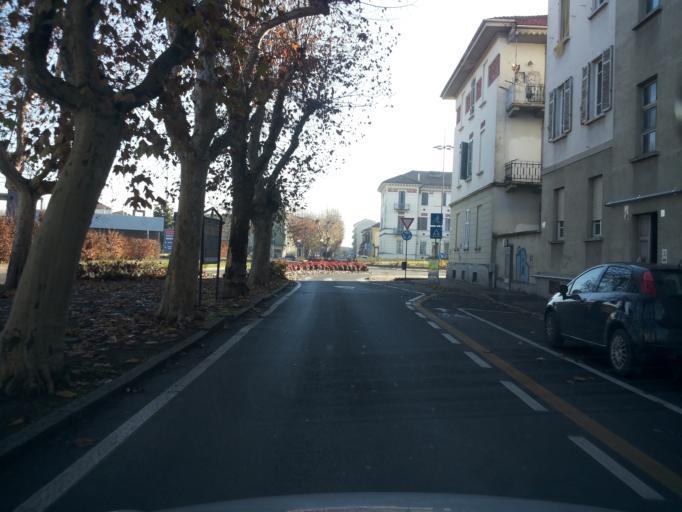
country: IT
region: Piedmont
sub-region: Provincia di Vercelli
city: Vercelli
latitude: 45.3301
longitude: 8.4307
